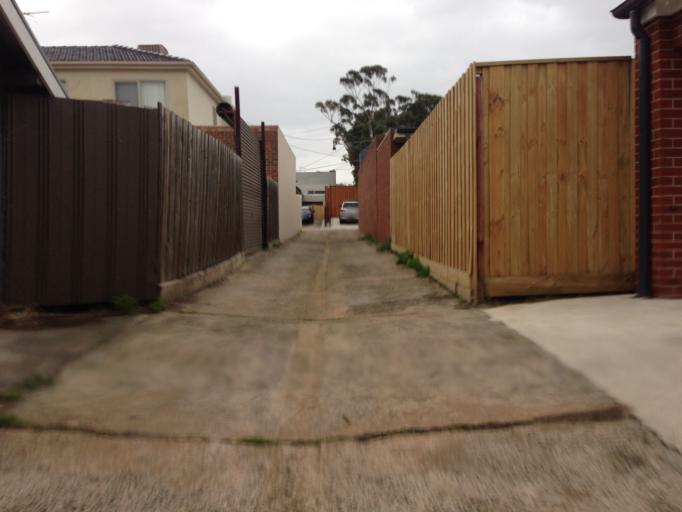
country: AU
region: Victoria
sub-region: Darebin
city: Fairfield
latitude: -37.7729
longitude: 145.0141
